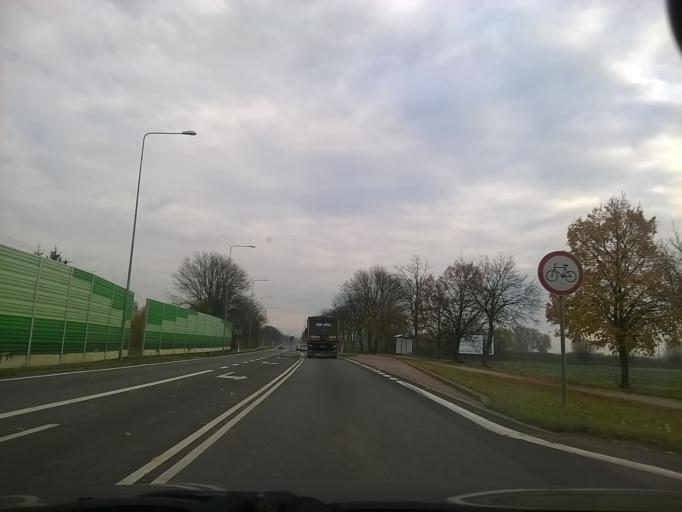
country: PL
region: Warmian-Masurian Voivodeship
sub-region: Powiat elblaski
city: Gronowo Elblaskie
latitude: 54.1676
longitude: 19.2705
